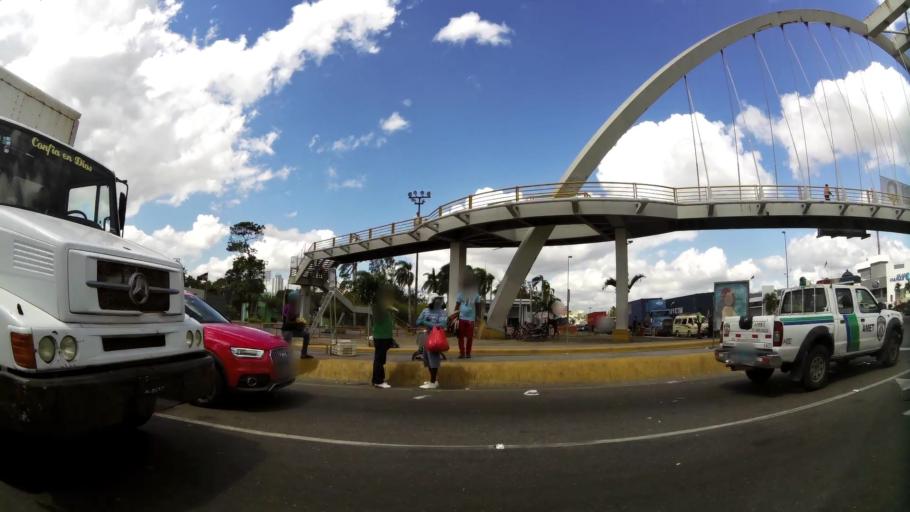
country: DO
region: Nacional
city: San Carlos
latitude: 18.4815
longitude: -69.9142
